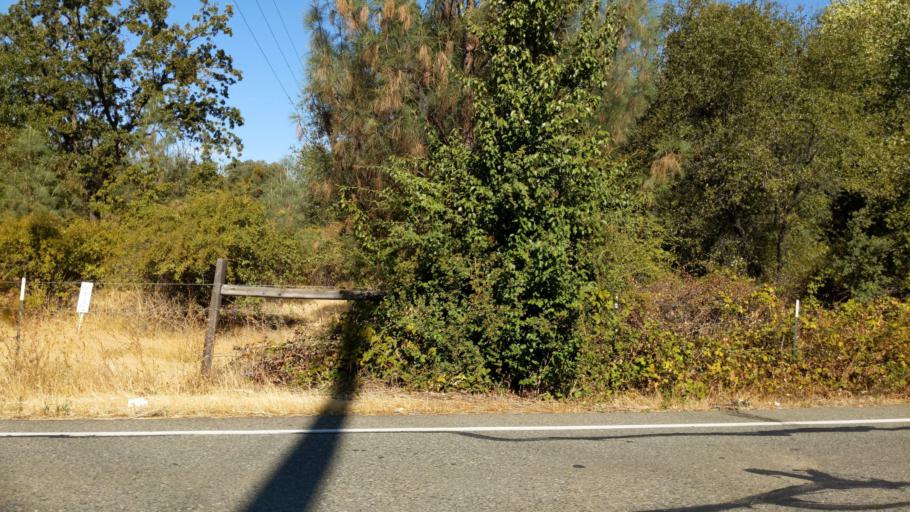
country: US
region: California
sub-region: Placer County
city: North Auburn
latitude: 38.9392
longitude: -121.0805
